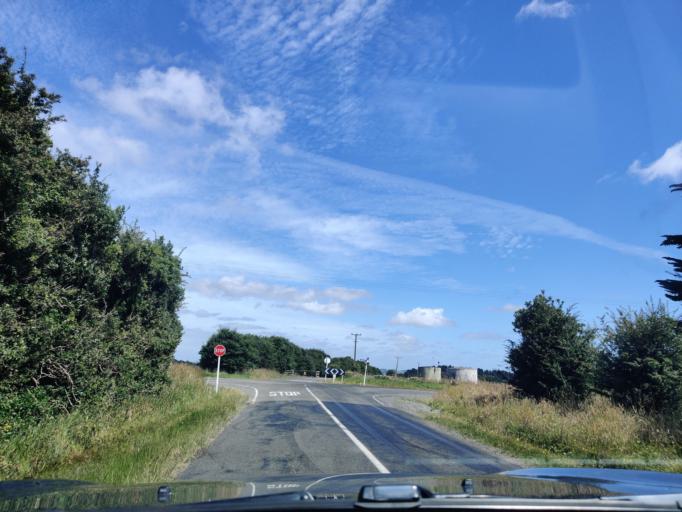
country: NZ
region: Manawatu-Wanganui
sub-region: Rangitikei District
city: Bulls
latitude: -40.1801
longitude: 175.4328
